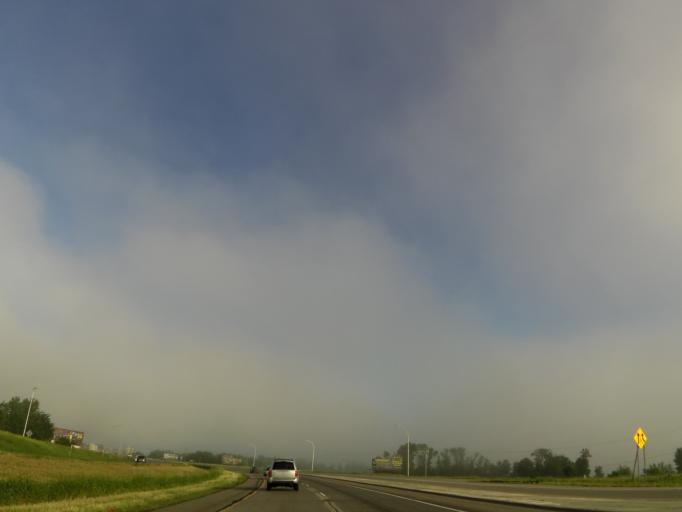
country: US
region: Minnesota
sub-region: Wright County
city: Albertville
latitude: 45.2386
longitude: -93.6498
